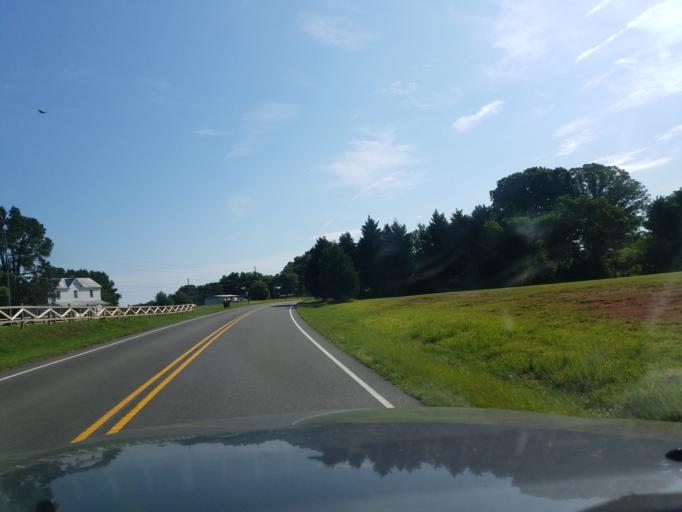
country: US
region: North Carolina
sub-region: Granville County
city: Butner
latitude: 36.2260
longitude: -78.7194
